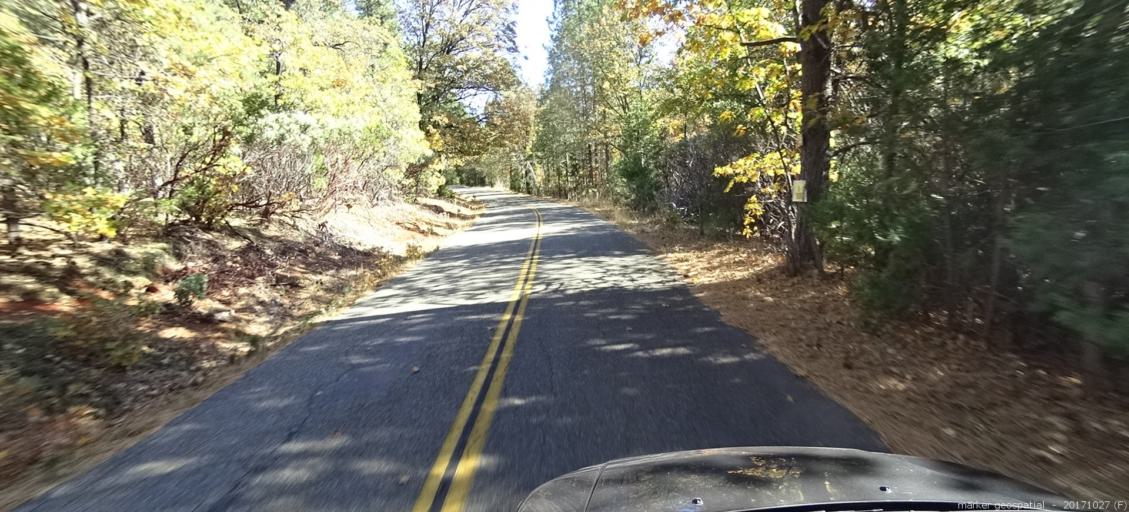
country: US
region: California
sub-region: Shasta County
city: Bella Vista
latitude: 40.7175
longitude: -121.9961
